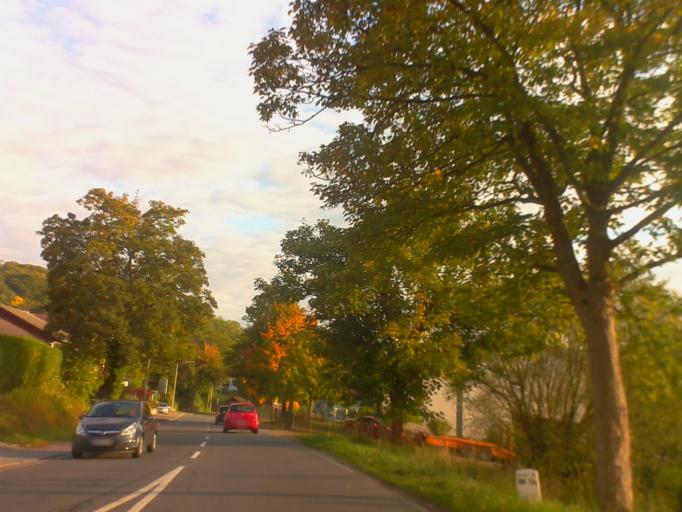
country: DE
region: Hesse
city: Reichelsheim
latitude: 49.7212
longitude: 8.8376
